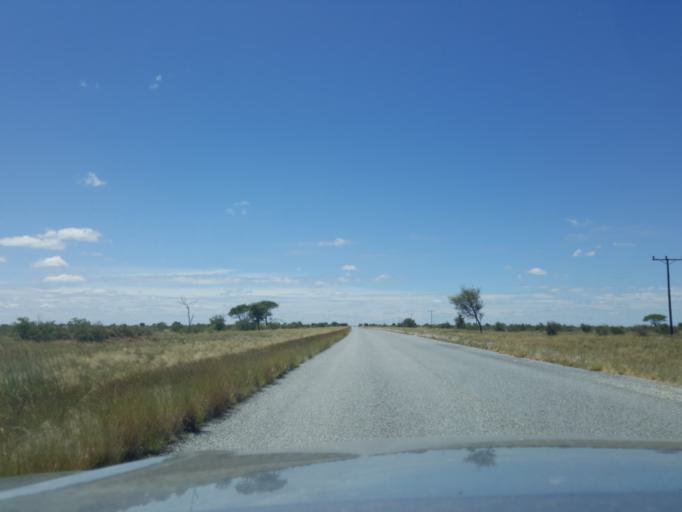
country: BW
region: Central
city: Nata
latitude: -20.1960
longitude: 26.0971
